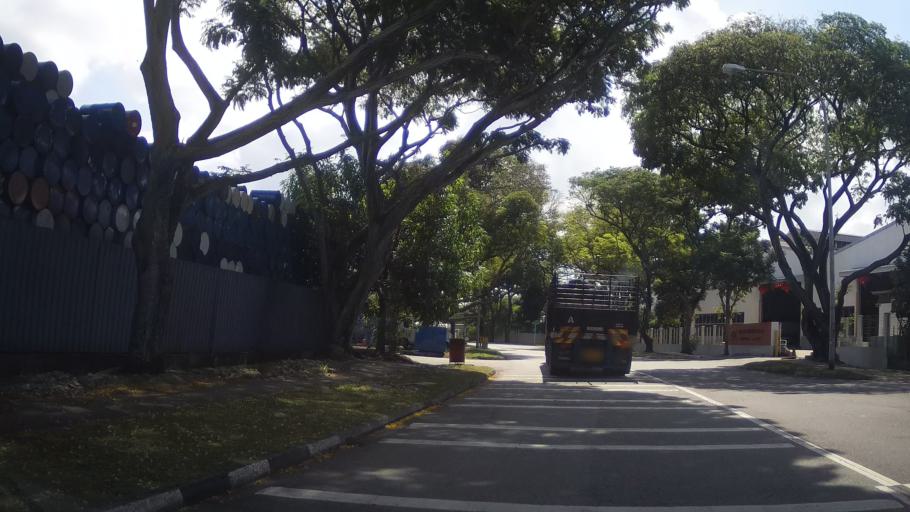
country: MY
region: Johor
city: Johor Bahru
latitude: 1.3095
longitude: 103.6640
